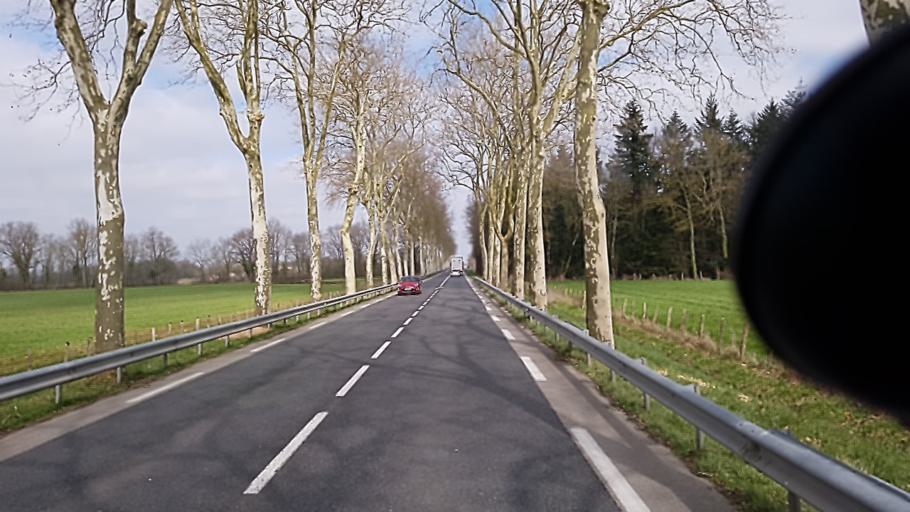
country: FR
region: Rhone-Alpes
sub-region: Departement de l'Ain
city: Saint-Paul-de-Varax
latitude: 46.0807
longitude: 5.1024
